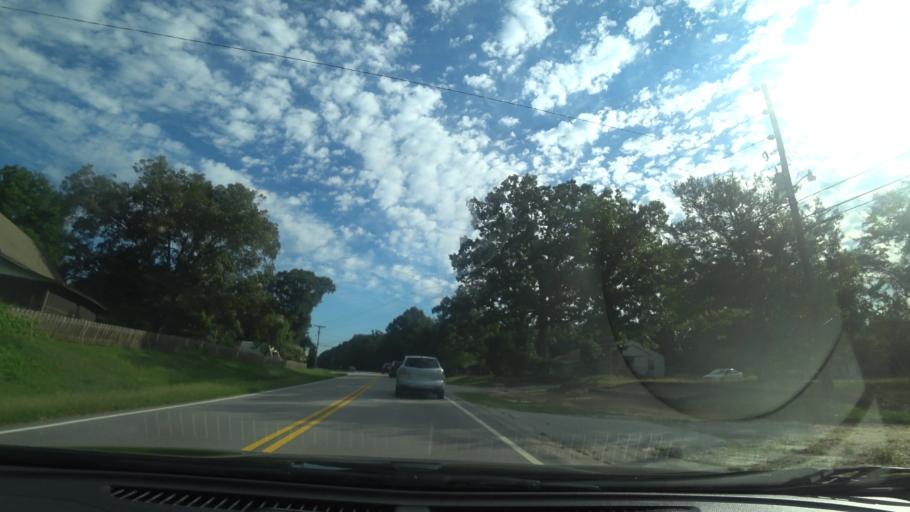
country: US
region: Georgia
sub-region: Rockdale County
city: Lakeview Estates
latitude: 33.7450
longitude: -83.9876
